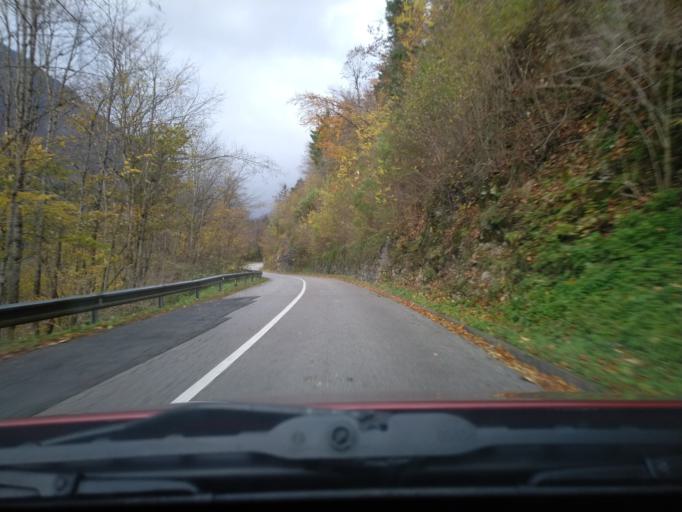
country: SI
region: Kamnik
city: Mekinje
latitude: 46.3018
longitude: 14.6097
